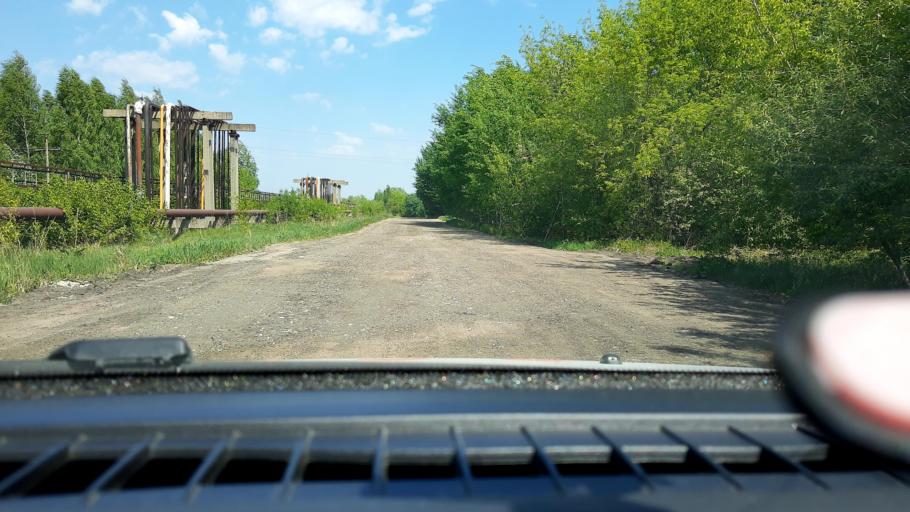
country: RU
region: Nizjnij Novgorod
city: Kstovo
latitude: 56.1281
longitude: 44.1268
